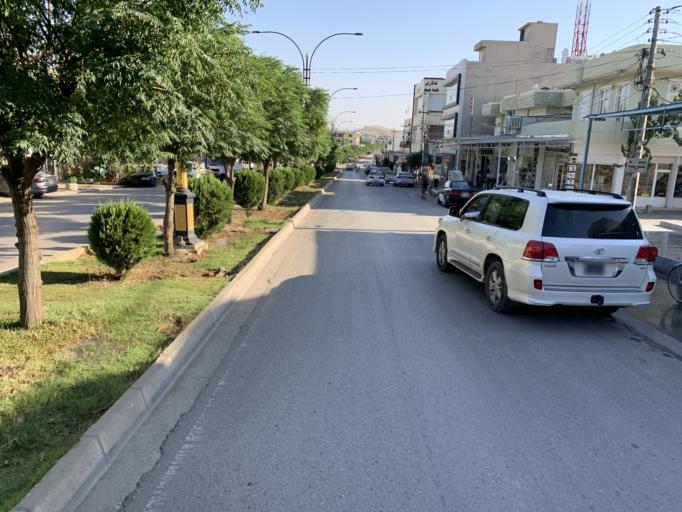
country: IQ
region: As Sulaymaniyah
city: Raniye
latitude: 36.2486
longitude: 44.8757
